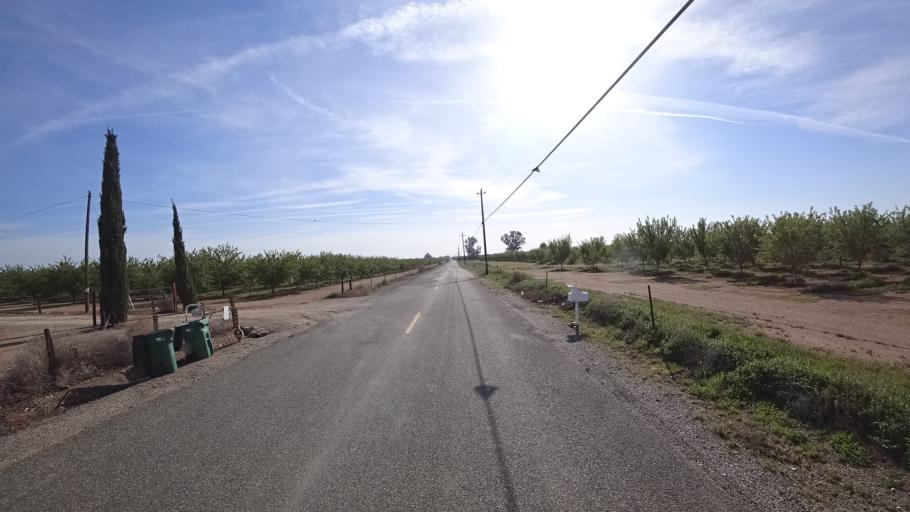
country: US
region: California
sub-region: Glenn County
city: Orland
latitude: 39.6683
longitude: -122.2581
